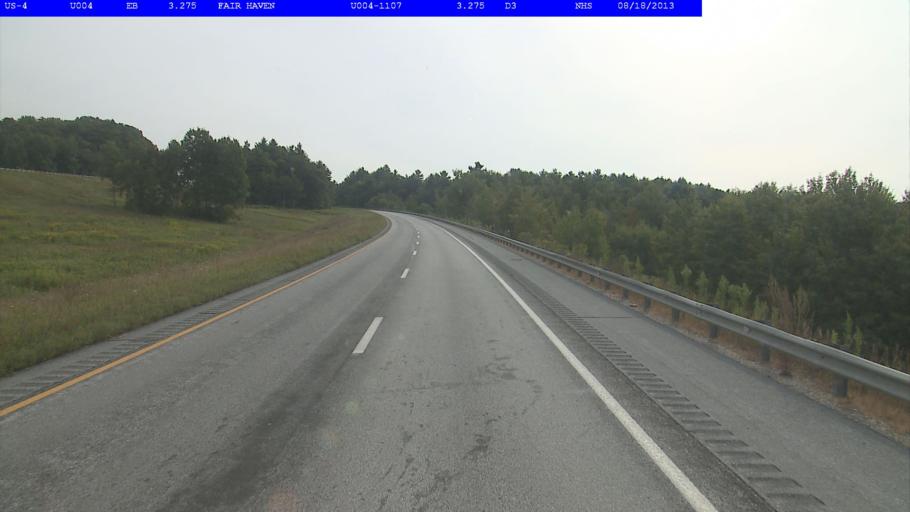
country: US
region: Vermont
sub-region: Rutland County
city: Fair Haven
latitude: 43.6050
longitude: -73.2462
